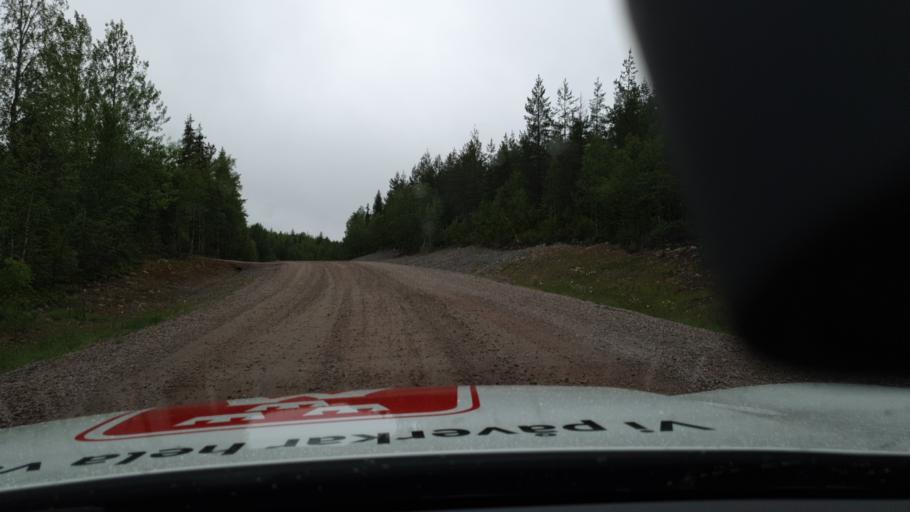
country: SE
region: Norrbotten
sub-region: Overtornea Kommun
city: OEvertornea
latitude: 66.5067
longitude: 23.4125
